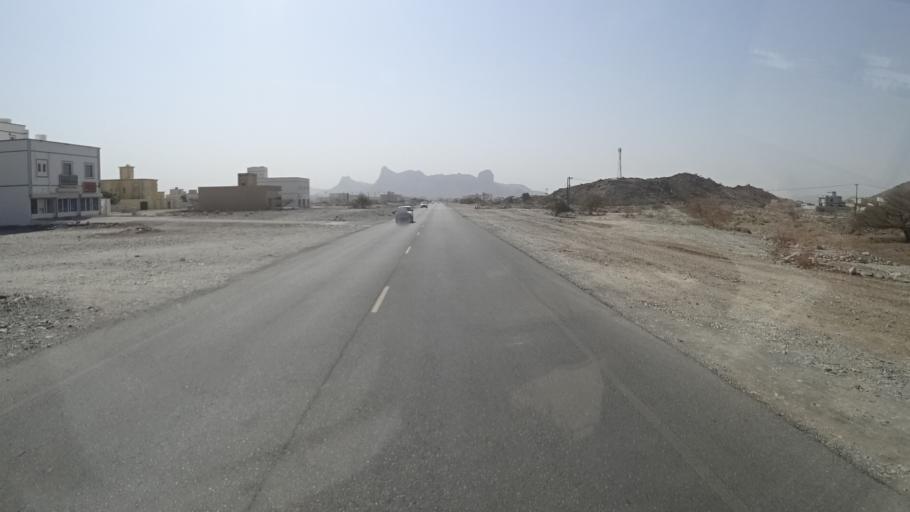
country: OM
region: Muhafazat ad Dakhiliyah
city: Bahla'
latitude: 23.1225
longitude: 57.2593
